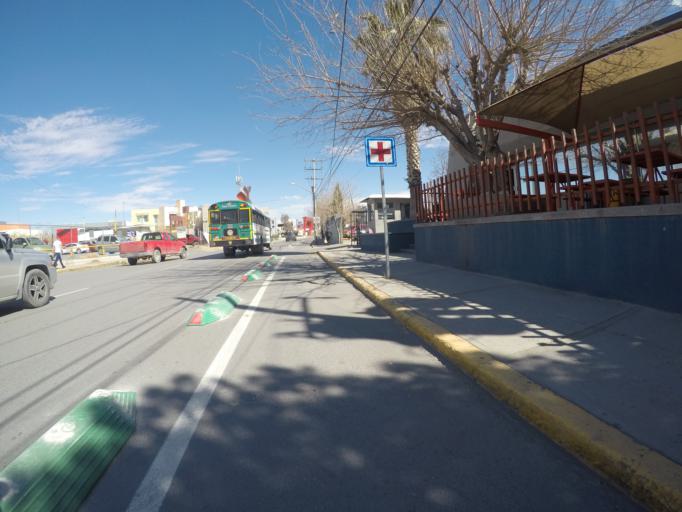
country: MX
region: Chihuahua
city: Ciudad Juarez
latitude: 31.7412
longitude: -106.4466
